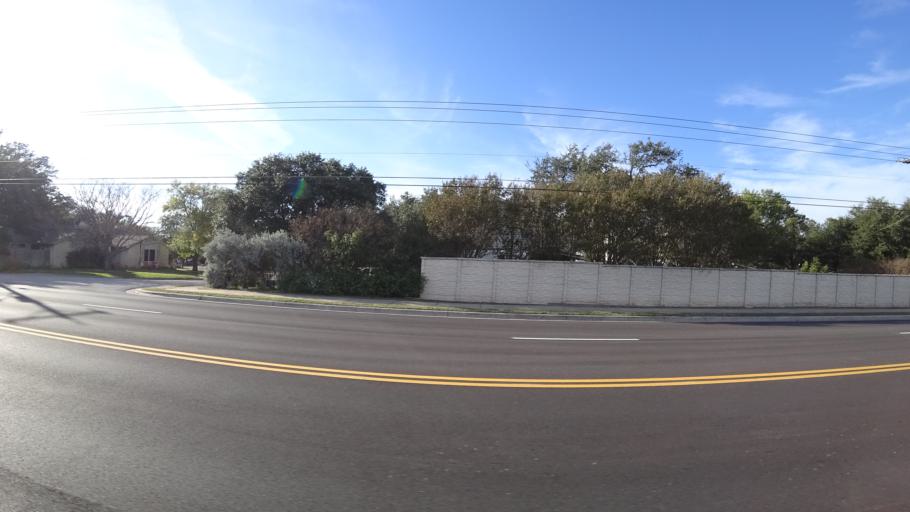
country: US
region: Texas
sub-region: Williamson County
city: Round Rock
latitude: 30.4837
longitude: -97.7012
